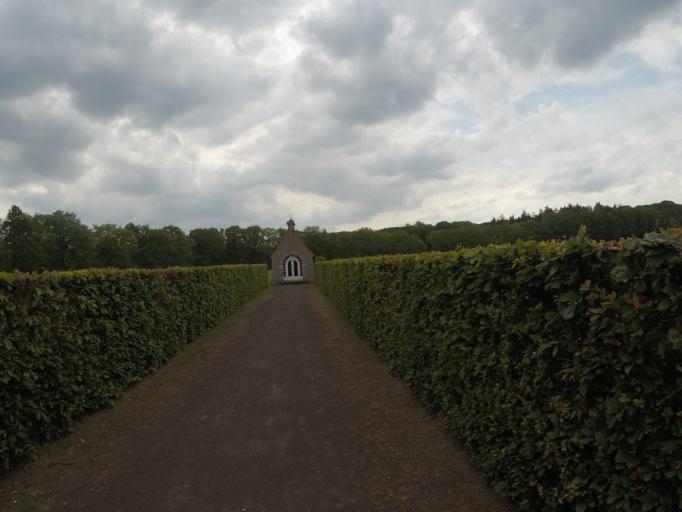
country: BE
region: Flanders
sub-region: Provincie Antwerpen
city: Zoersel
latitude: 51.2811
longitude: 4.6588
